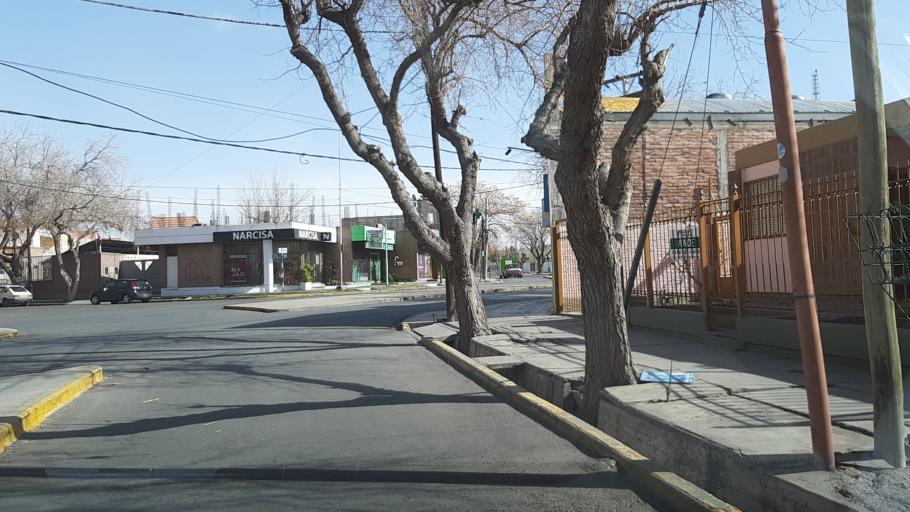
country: AR
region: San Juan
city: San Juan
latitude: -31.5274
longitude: -68.5483
